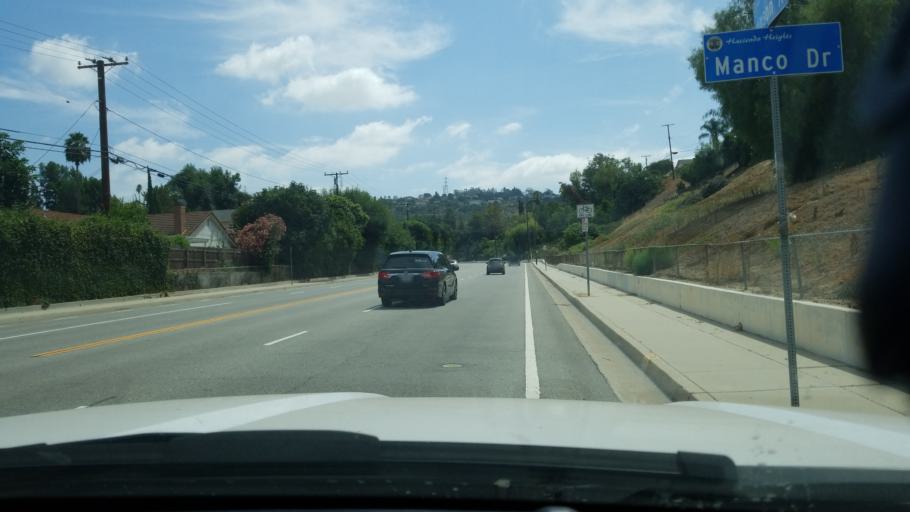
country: US
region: California
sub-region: Los Angeles County
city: Hacienda Heights
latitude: 33.9892
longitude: -117.9646
